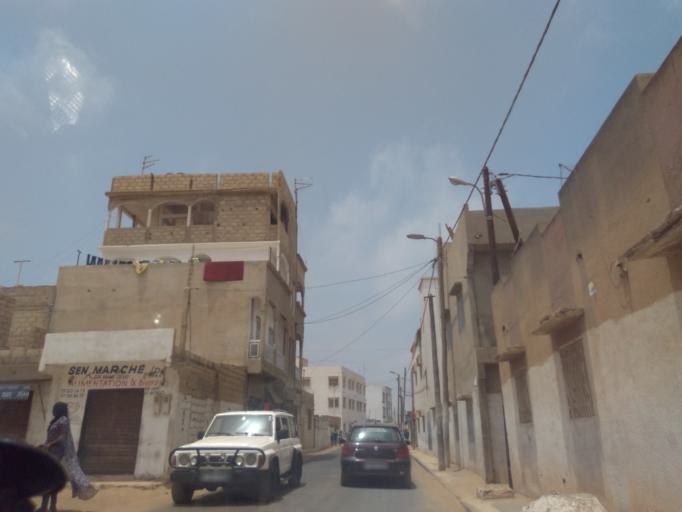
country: SN
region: Dakar
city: Pikine
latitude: 14.7701
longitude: -17.4289
